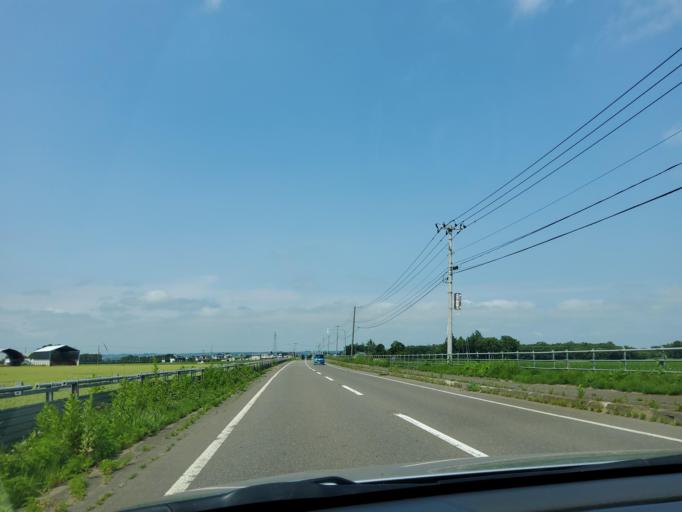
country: JP
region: Hokkaido
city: Obihiro
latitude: 42.8928
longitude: 143.0412
